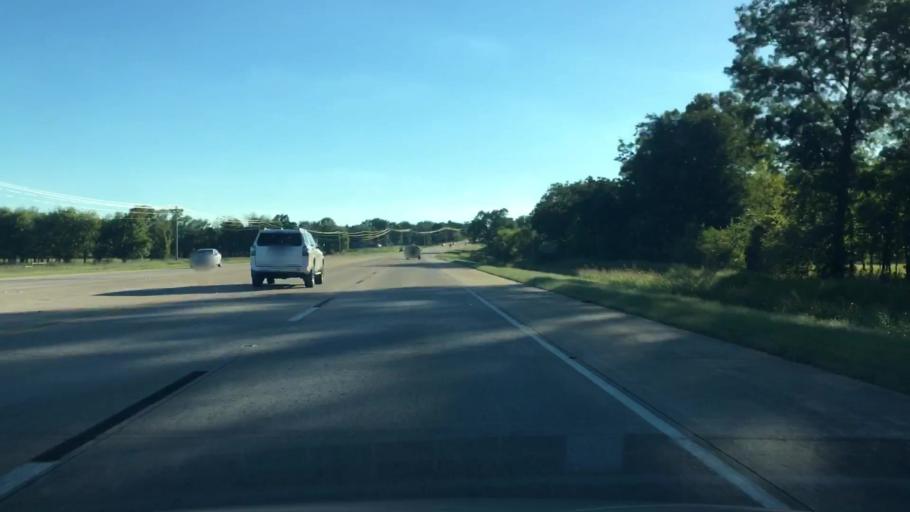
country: US
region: Oklahoma
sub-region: Cherokee County
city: Park Hill
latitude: 35.8232
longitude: -95.0508
